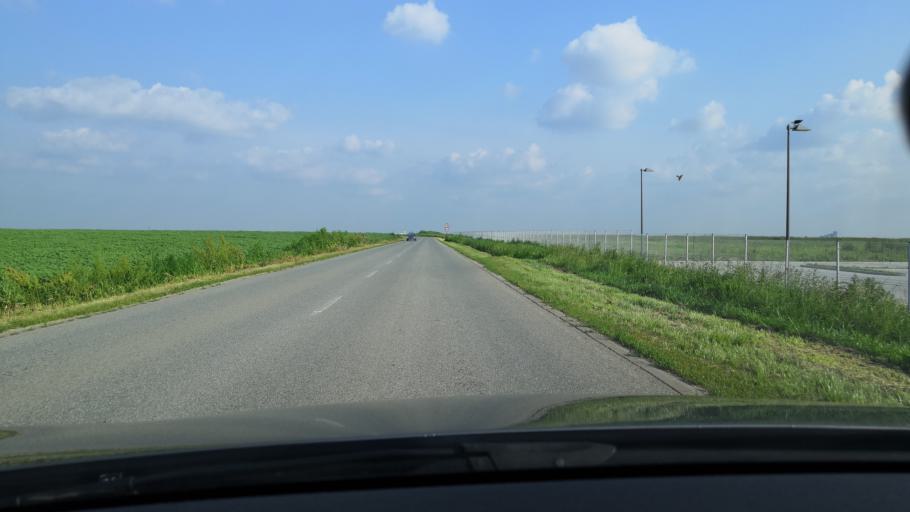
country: RS
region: Autonomna Pokrajina Vojvodina
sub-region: Sremski Okrug
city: Ingija
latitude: 45.0929
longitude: 20.0962
